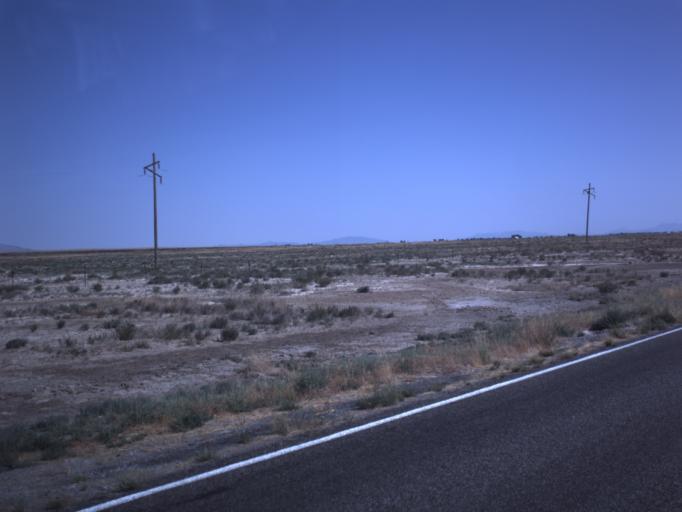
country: US
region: Utah
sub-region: Millard County
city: Delta
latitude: 39.1969
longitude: -112.6900
